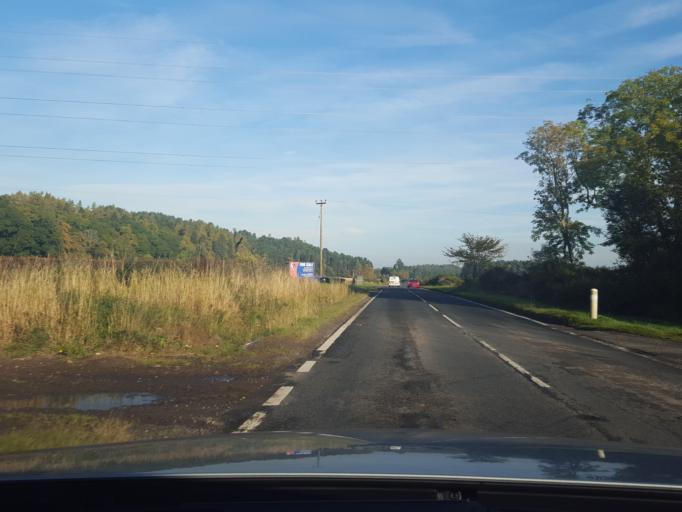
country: GB
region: Scotland
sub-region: Highland
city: Inverness
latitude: 57.4475
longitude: -4.2884
